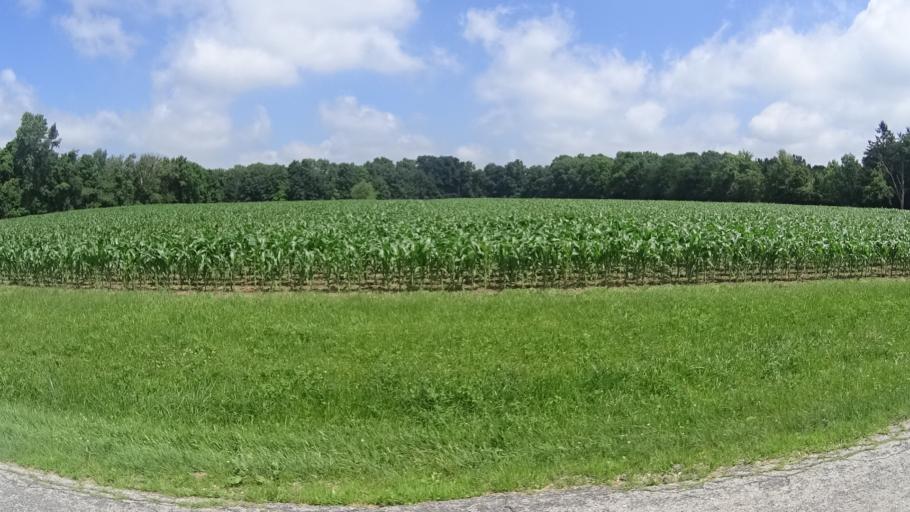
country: US
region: Ohio
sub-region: Huron County
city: Wakeman
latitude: 41.2985
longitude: -82.3499
